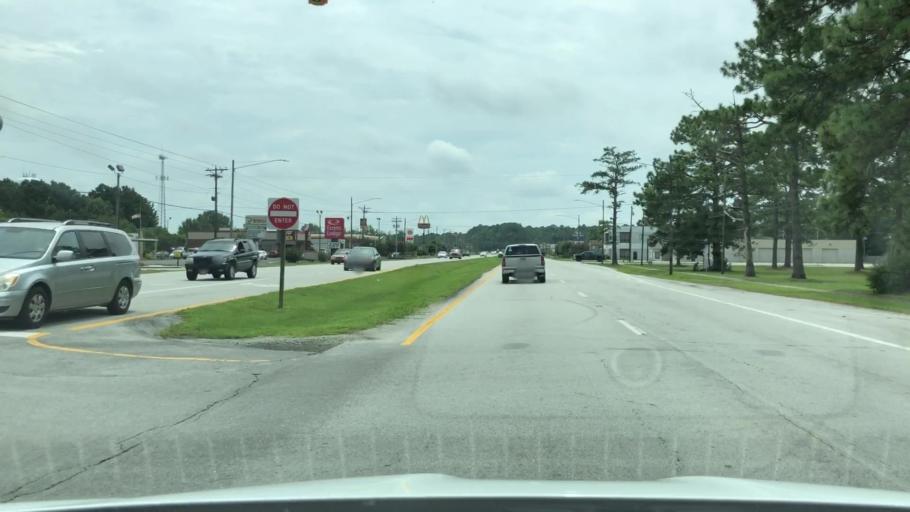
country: US
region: North Carolina
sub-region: Craven County
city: Havelock
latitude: 34.8634
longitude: -76.8984
